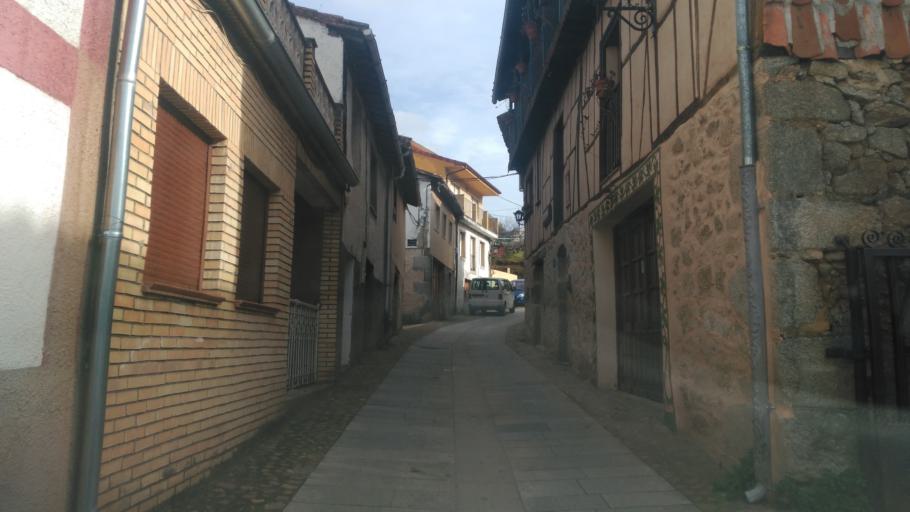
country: ES
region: Castille and Leon
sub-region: Provincia de Salamanca
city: San Esteban de la Sierra
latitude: 40.5058
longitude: -5.9065
